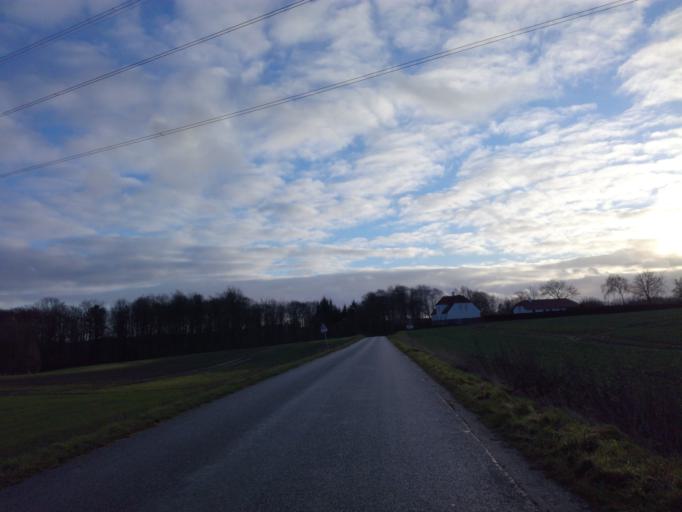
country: DK
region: South Denmark
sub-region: Fredericia Kommune
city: Taulov
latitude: 55.5544
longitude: 9.6025
